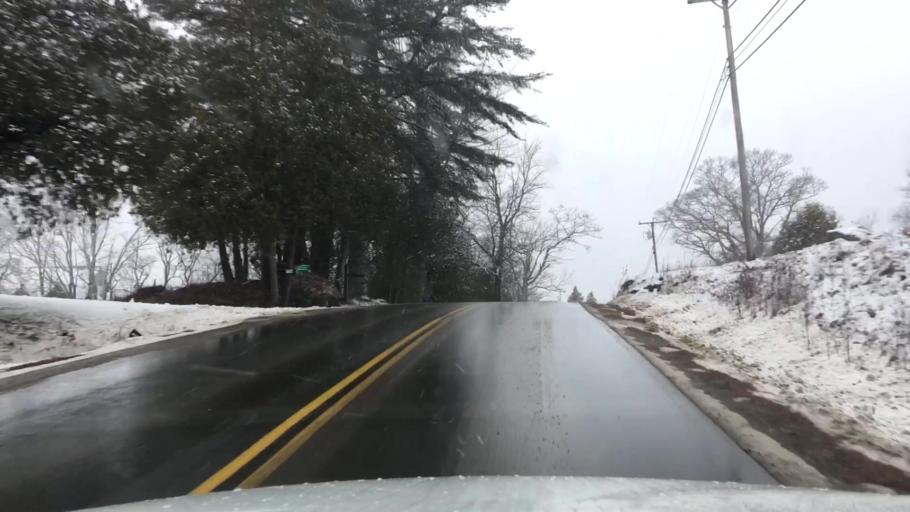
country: US
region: Maine
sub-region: Knox County
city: Warren
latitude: 44.1278
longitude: -69.2554
